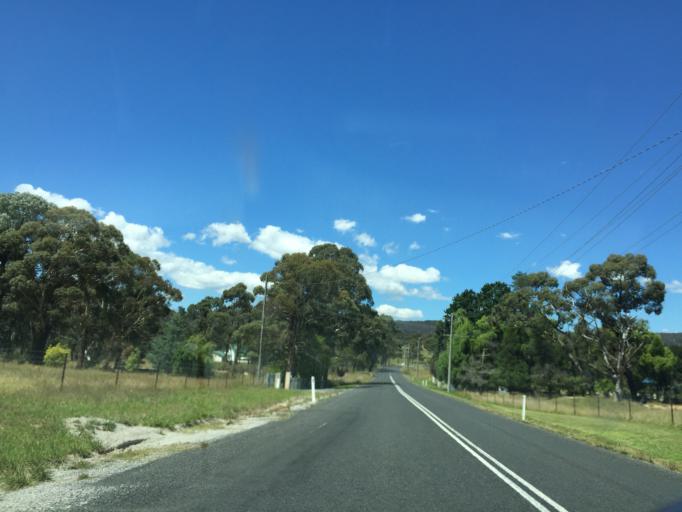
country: AU
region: New South Wales
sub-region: Lithgow
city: Lithgow
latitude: -33.4381
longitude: 150.1222
